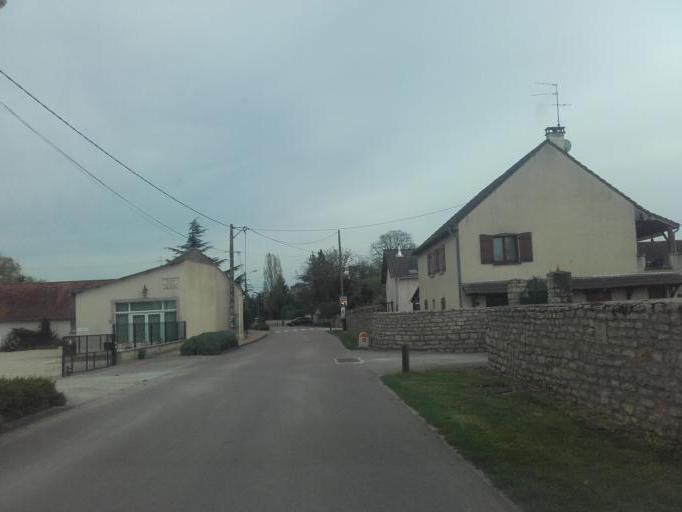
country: FR
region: Bourgogne
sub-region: Departement de Saone-et-Loire
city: Demigny
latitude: 46.9523
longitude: 4.8388
